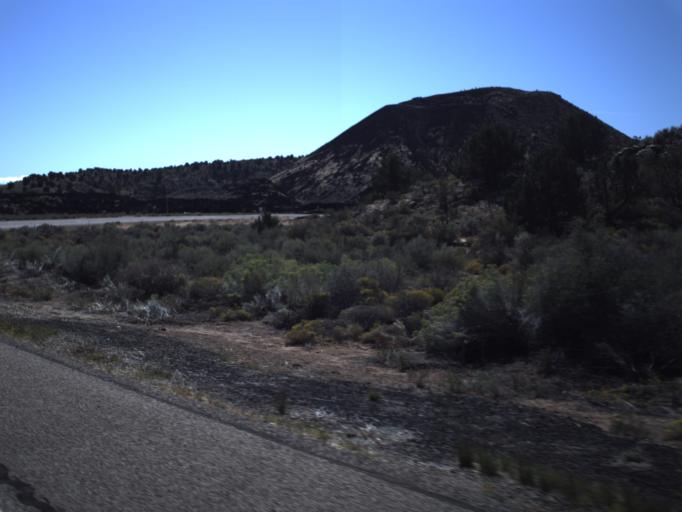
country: US
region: Utah
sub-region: Washington County
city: Ivins
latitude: 37.2505
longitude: -113.6279
